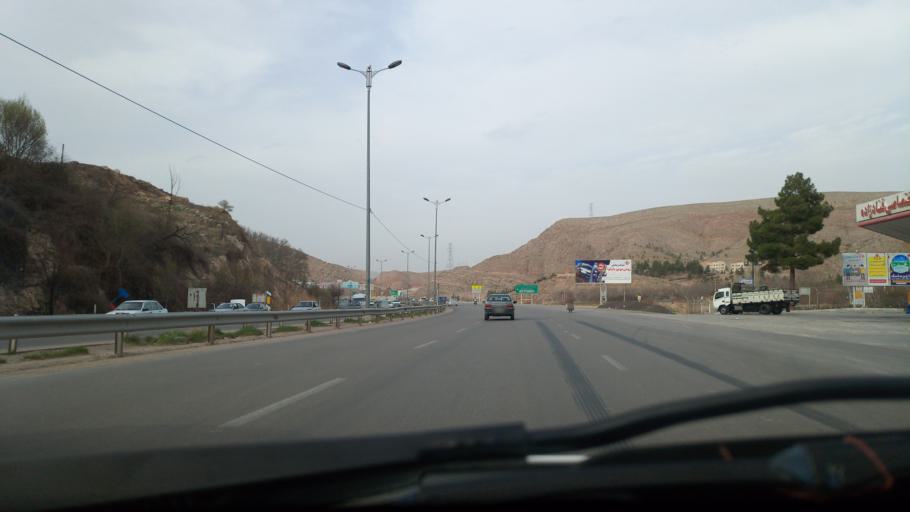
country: IR
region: Khorasan-e Shomali
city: Bojnurd
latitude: 37.4818
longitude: 57.4366
